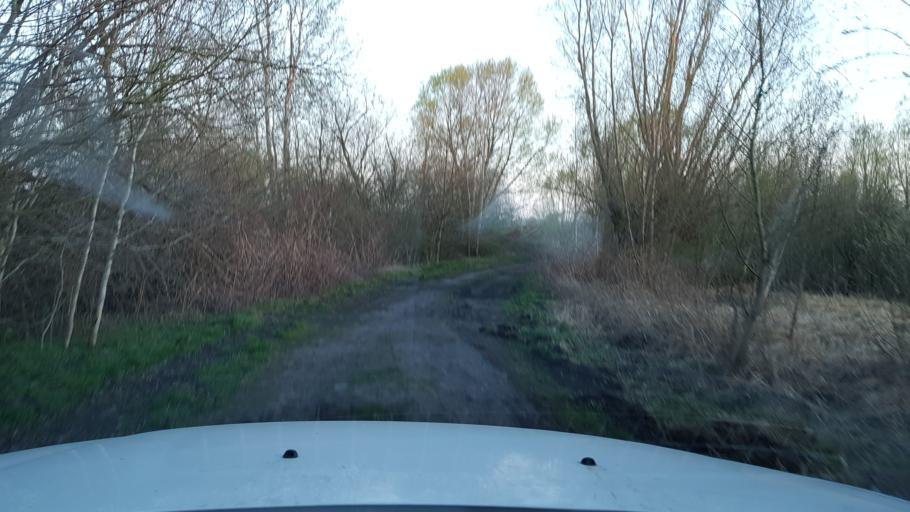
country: PL
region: West Pomeranian Voivodeship
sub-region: Powiat bialogardzki
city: Bialogard
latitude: 53.9754
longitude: 15.9570
